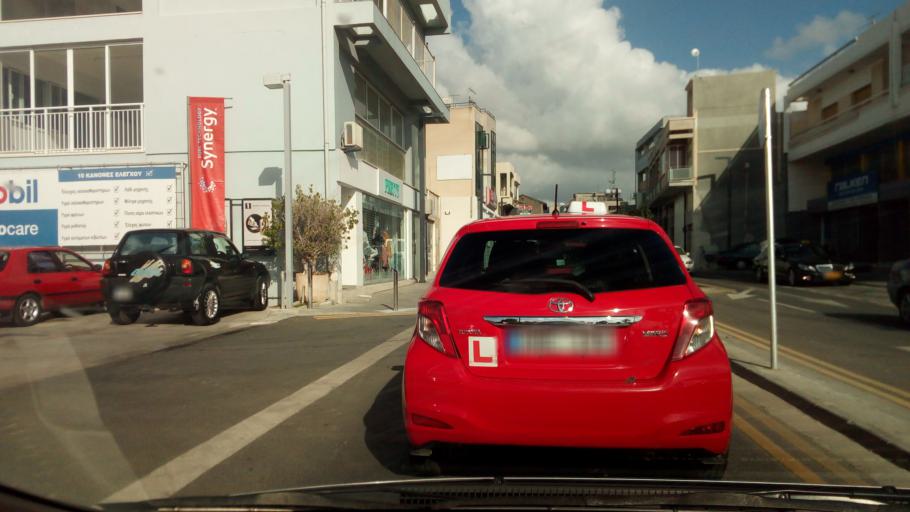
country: CY
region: Pafos
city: Paphos
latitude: 34.7780
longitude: 32.4239
